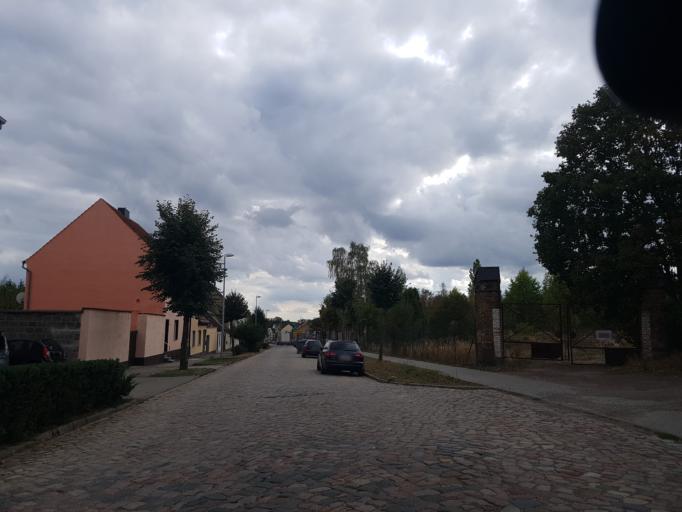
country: DE
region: Saxony-Anhalt
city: Coswig
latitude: 51.8868
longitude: 12.4495
